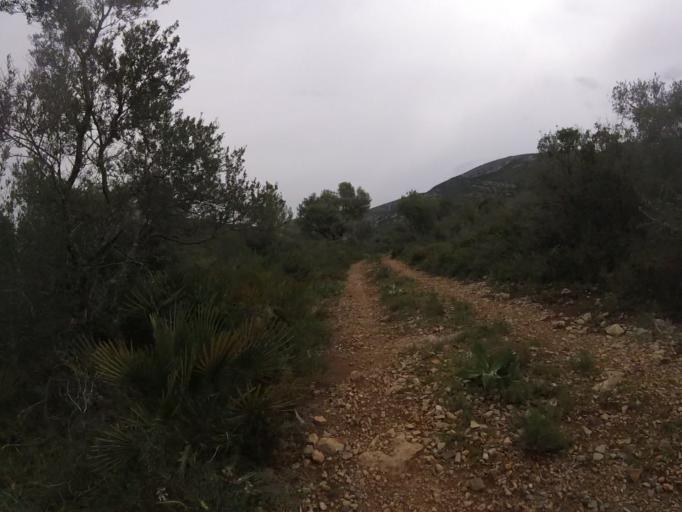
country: ES
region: Valencia
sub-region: Provincia de Castello
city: Santa Magdalena de Pulpis
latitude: 40.3702
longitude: 0.3333
